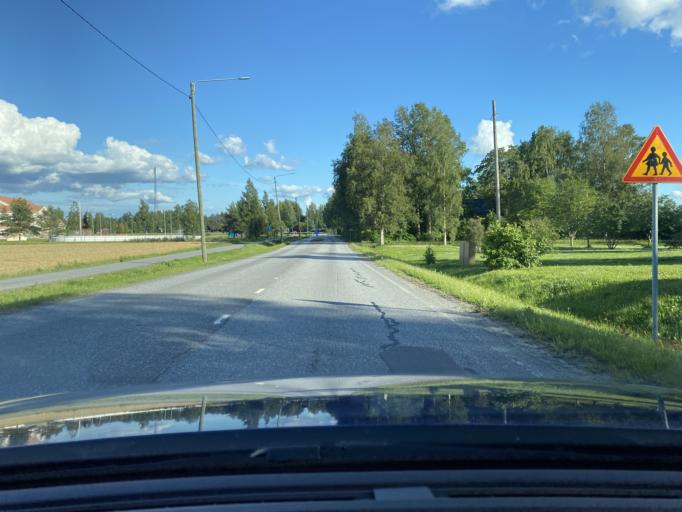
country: FI
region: Ostrobothnia
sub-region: Kyroenmaa
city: Laihia
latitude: 62.9806
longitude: 21.9953
